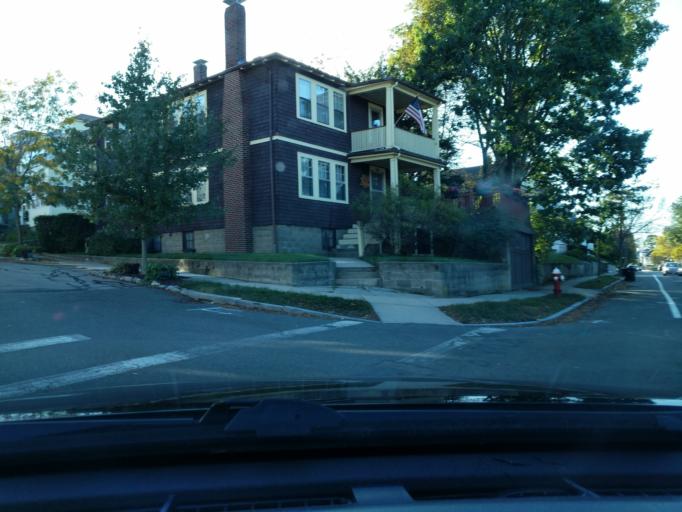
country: US
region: Massachusetts
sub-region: Middlesex County
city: Watertown
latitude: 42.3803
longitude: -71.1821
